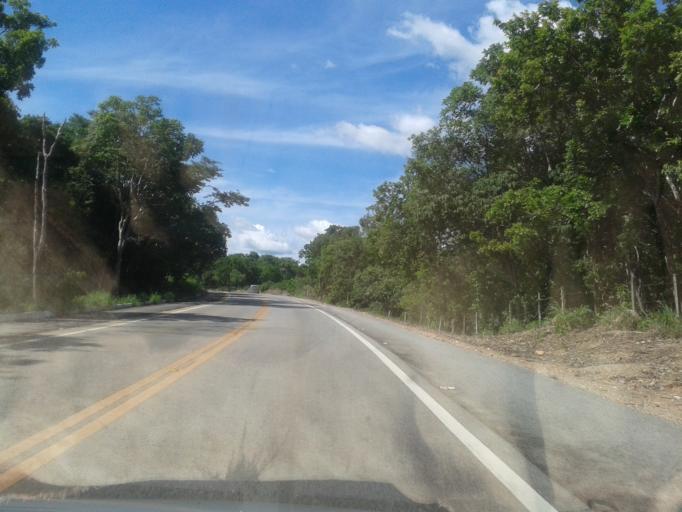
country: BR
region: Goias
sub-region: Itapuranga
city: Itapuranga
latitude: -15.3740
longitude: -50.3874
